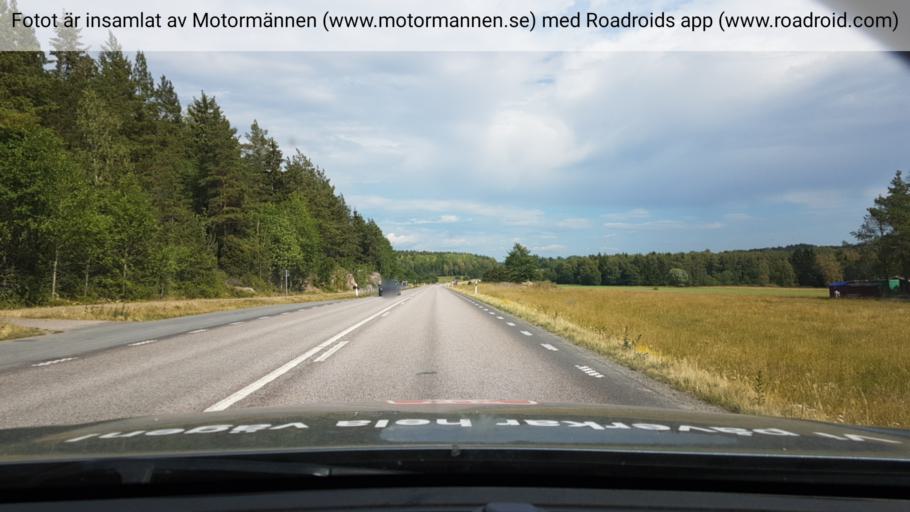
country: SE
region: Uppsala
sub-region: Uppsala Kommun
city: Uppsala
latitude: 59.8514
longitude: 17.4910
